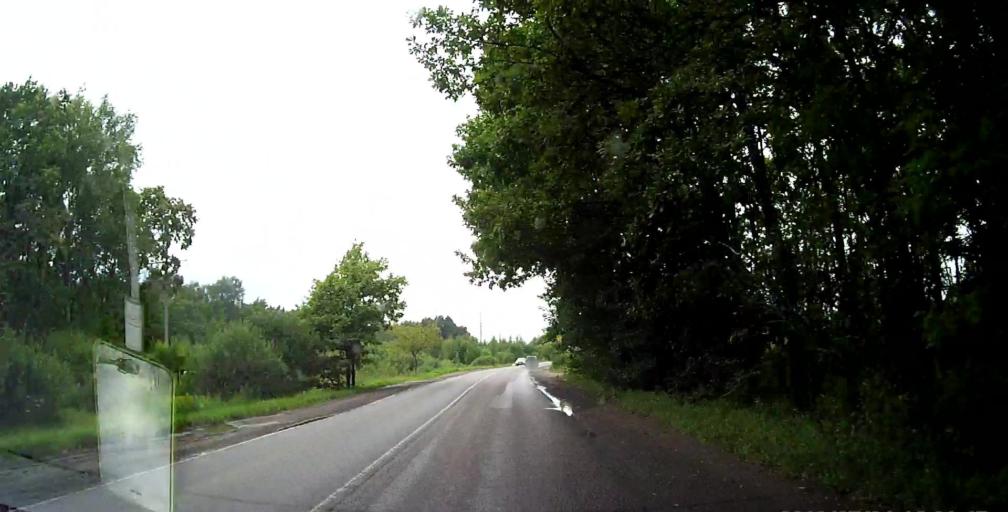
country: RU
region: Moskovskaya
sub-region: Podol'skiy Rayon
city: Podol'sk
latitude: 55.3868
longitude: 37.5627
